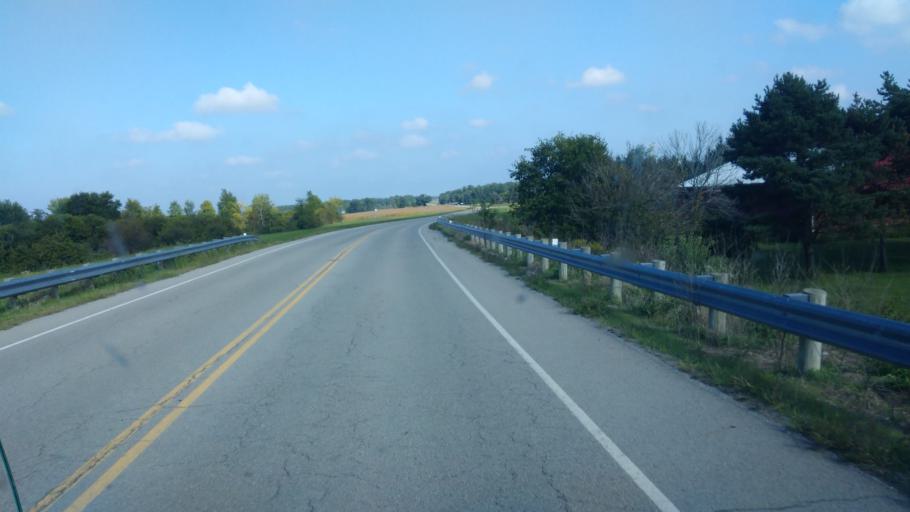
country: US
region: Ohio
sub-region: Hancock County
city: Arlington
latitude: 40.8346
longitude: -83.6466
